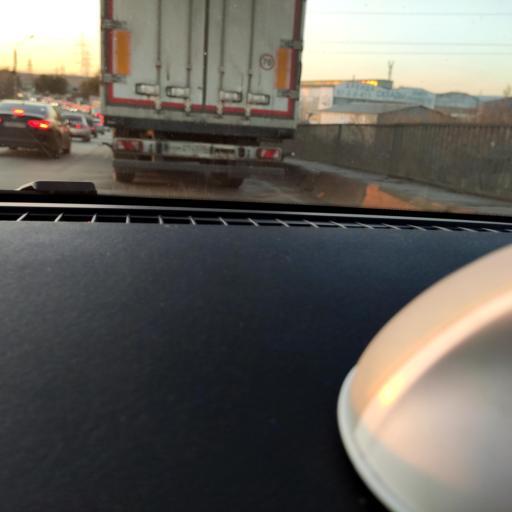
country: RU
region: Samara
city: Petra-Dubrava
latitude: 53.2562
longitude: 50.3040
